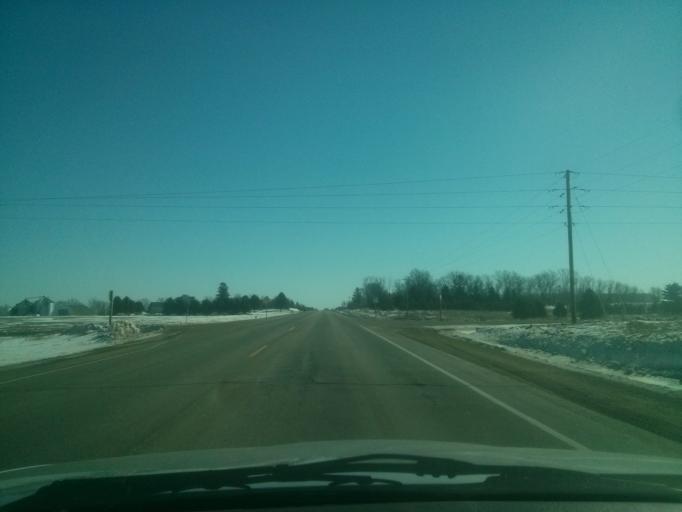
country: US
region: Wisconsin
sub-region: Saint Croix County
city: New Richmond
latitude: 45.1370
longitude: -92.4674
